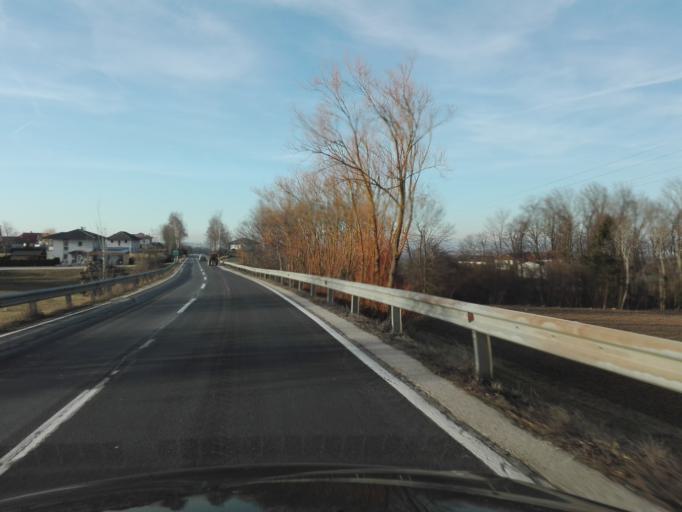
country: AT
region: Lower Austria
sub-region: Politischer Bezirk Amstetten
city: Strengberg
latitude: 48.1603
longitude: 14.6171
